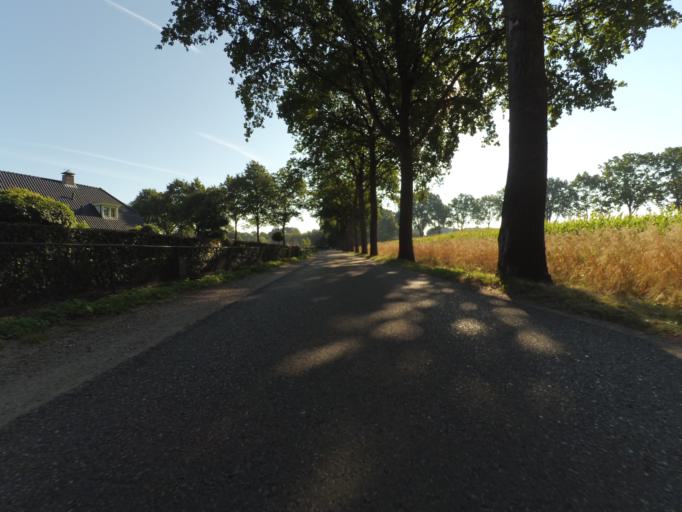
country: NL
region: Gelderland
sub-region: Gemeente Putten
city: Putten
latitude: 52.2492
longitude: 5.5858
